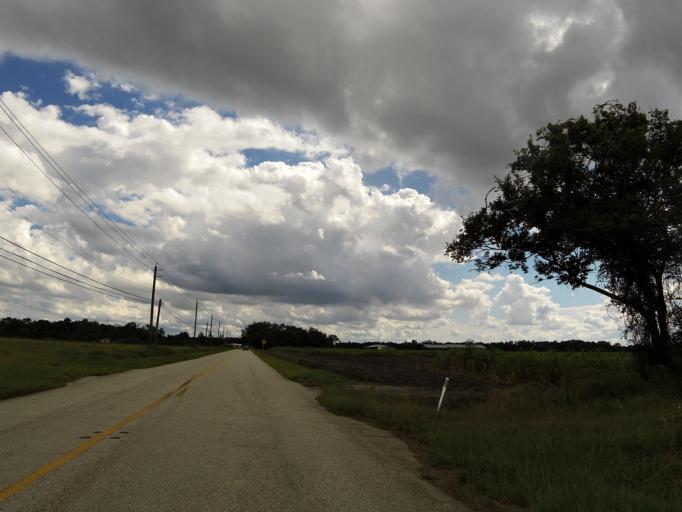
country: US
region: Florida
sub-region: Saint Johns County
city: Saint Augustine South
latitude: 29.8495
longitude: -81.4987
